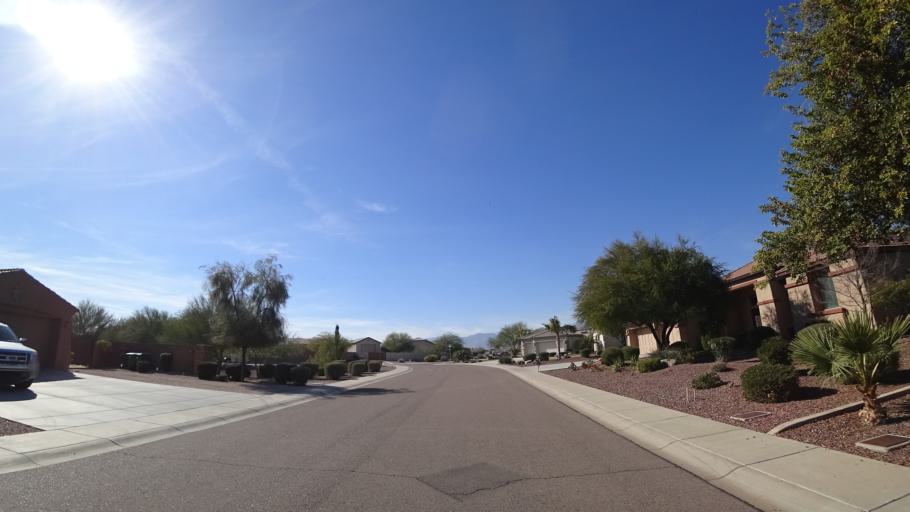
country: US
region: Arizona
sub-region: Maricopa County
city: Citrus Park
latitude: 33.5185
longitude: -112.4565
